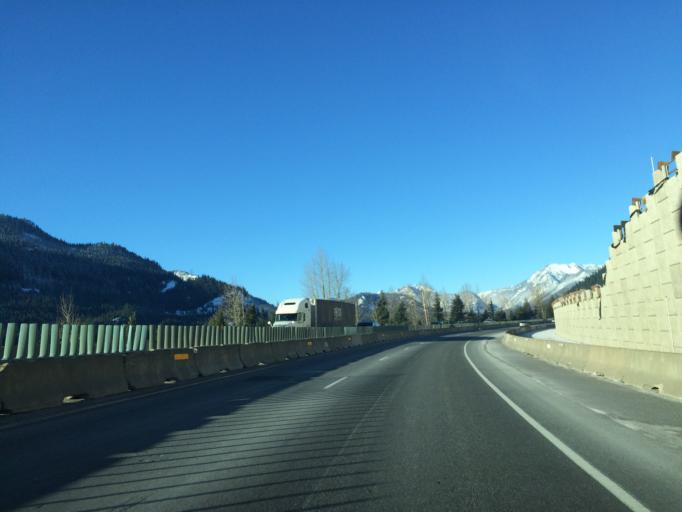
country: US
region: Washington
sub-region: King County
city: Tanner
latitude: 47.3425
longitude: -121.3635
